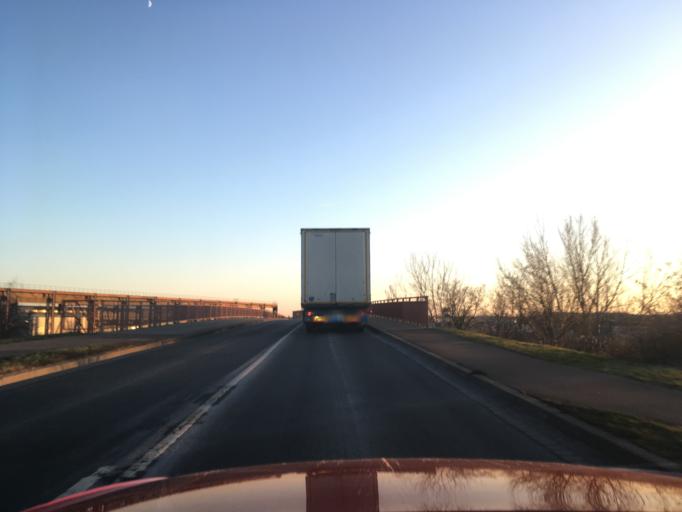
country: DE
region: Saxony-Anhalt
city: Dessau
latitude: 51.8315
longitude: 12.2140
